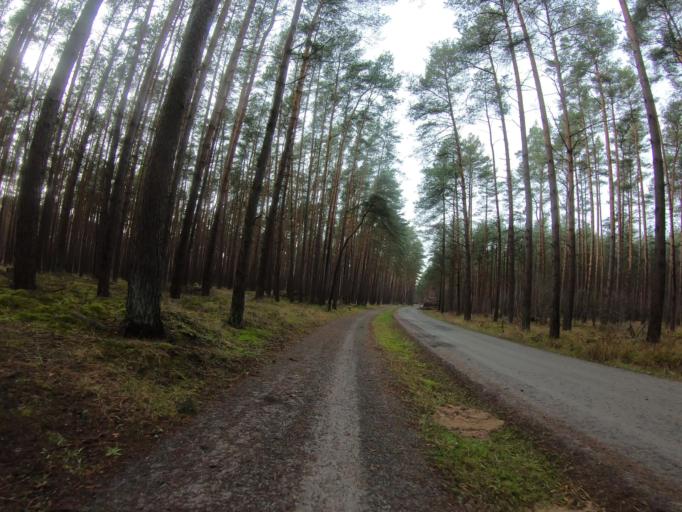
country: DE
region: Lower Saxony
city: Leiferde
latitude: 52.5089
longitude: 10.4307
